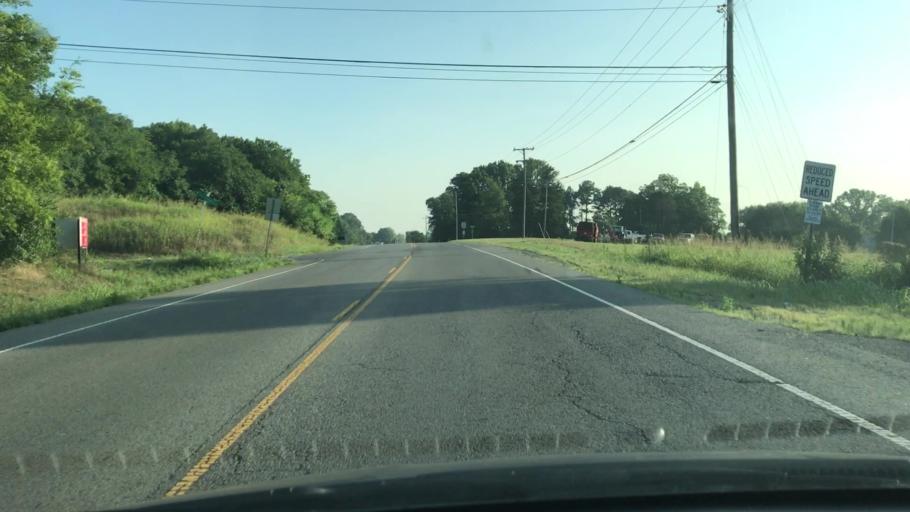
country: US
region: Tennessee
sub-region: Rutherford County
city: La Vergne
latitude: 36.0046
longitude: -86.6218
